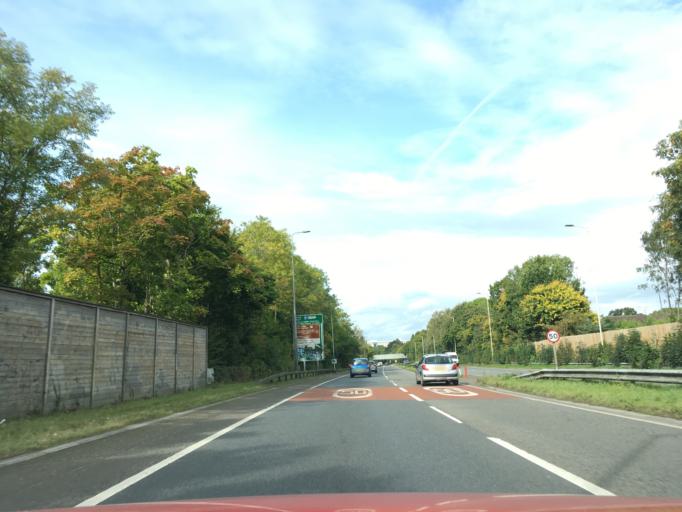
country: GB
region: Wales
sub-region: Cardiff
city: Cardiff
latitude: 51.5021
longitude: -3.1717
